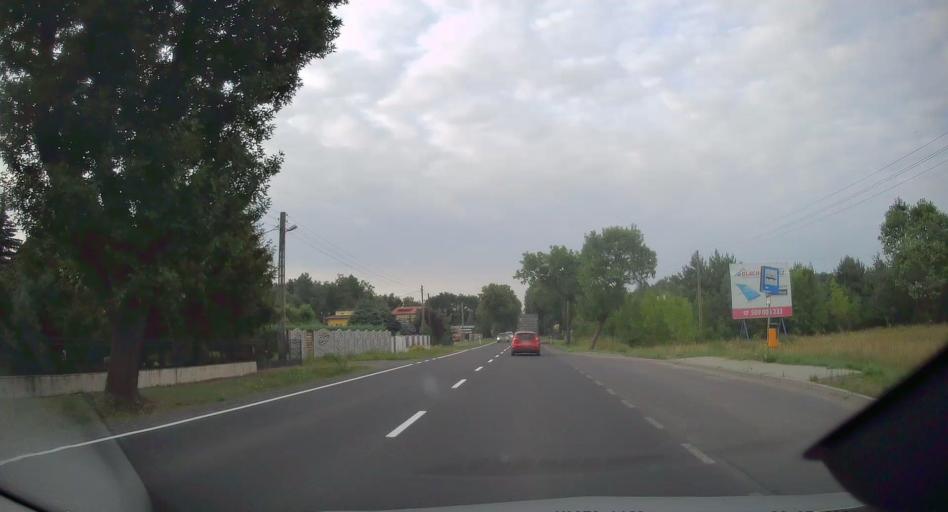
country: PL
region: Lodz Voivodeship
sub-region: Powiat radomszczanski
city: Radomsko
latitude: 51.1137
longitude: 19.4692
